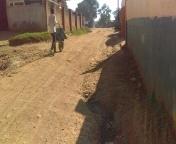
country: UG
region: Central Region
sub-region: Kampala District
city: Kampala
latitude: 0.2533
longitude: 32.5729
